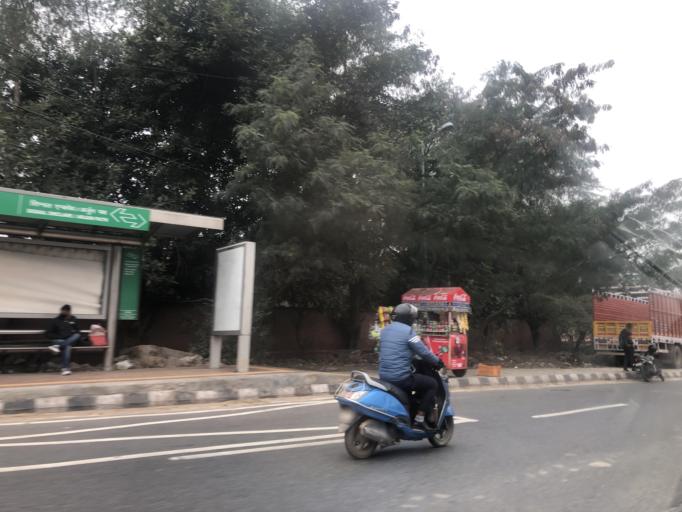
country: IN
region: NCT
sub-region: Central Delhi
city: Karol Bagh
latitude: 28.5740
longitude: 77.1517
